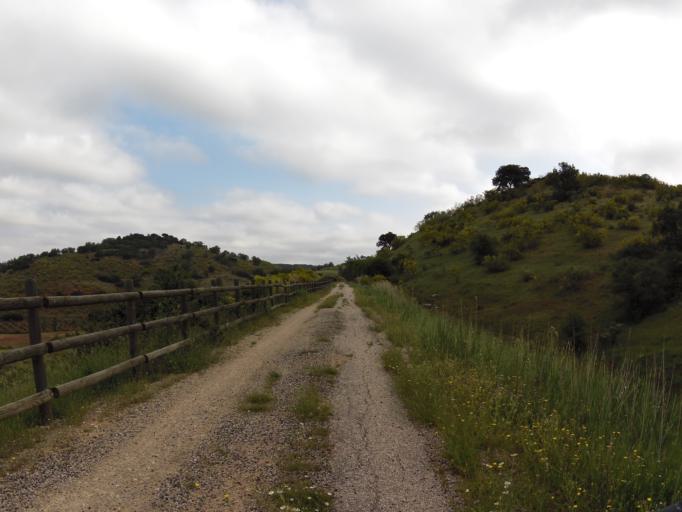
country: ES
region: Castille-La Mancha
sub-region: Provincia de Albacete
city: Alcaraz
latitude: 38.7065
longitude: -2.5009
